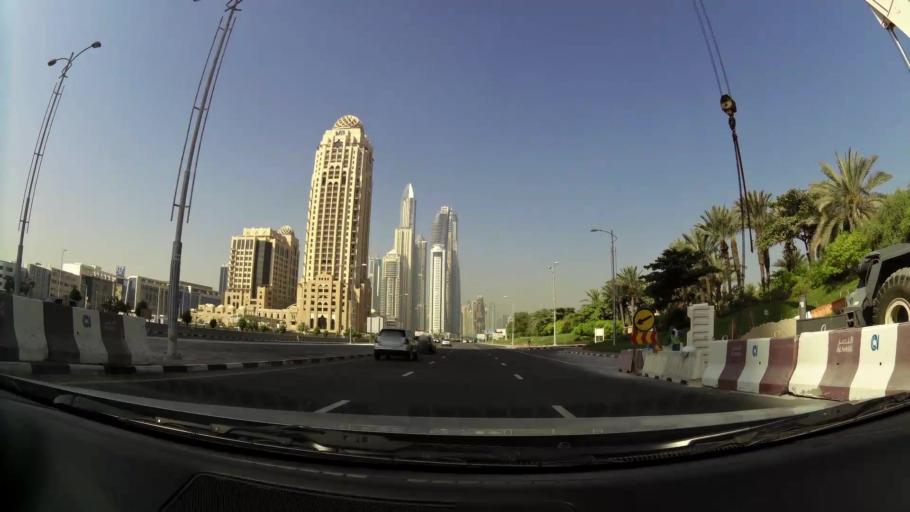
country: AE
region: Dubai
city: Dubai
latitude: 25.0980
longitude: 55.1548
